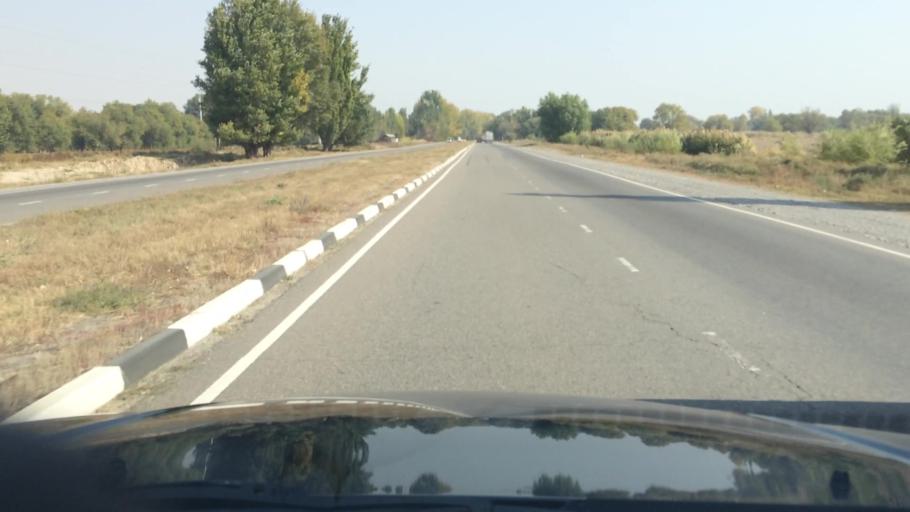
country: KG
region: Chuy
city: Kant
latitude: 42.9705
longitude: 74.8507
